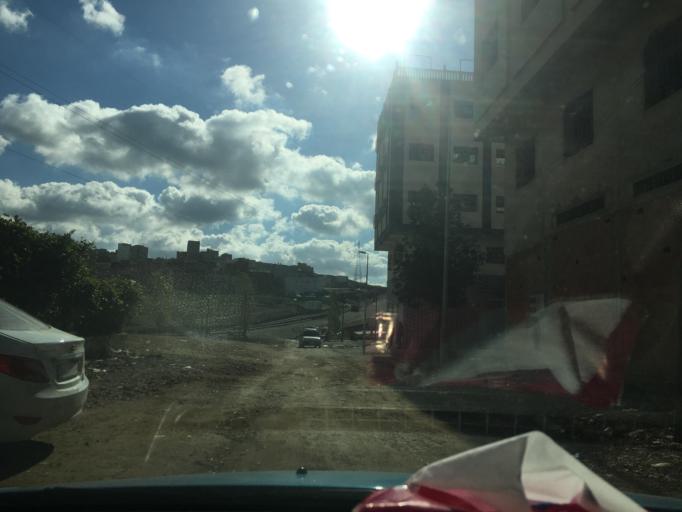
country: MA
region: Tanger-Tetouan
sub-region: Tanger-Assilah
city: Tangier
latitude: 35.7220
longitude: -5.8129
